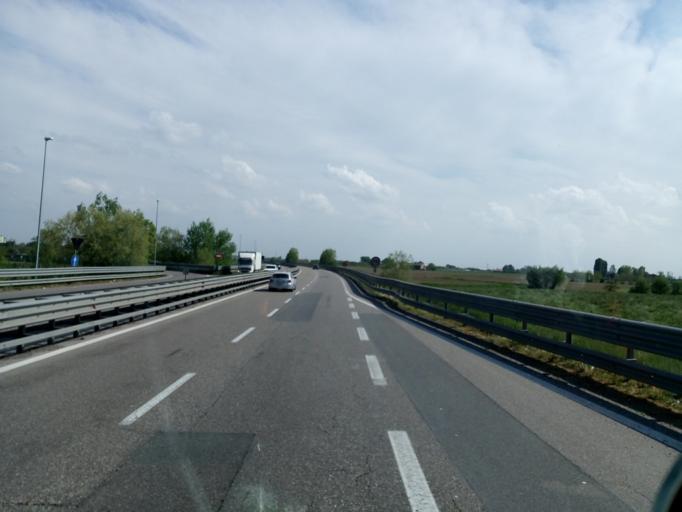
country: IT
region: Veneto
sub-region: Provincia di Verona
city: Legnago
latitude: 45.2068
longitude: 11.2470
